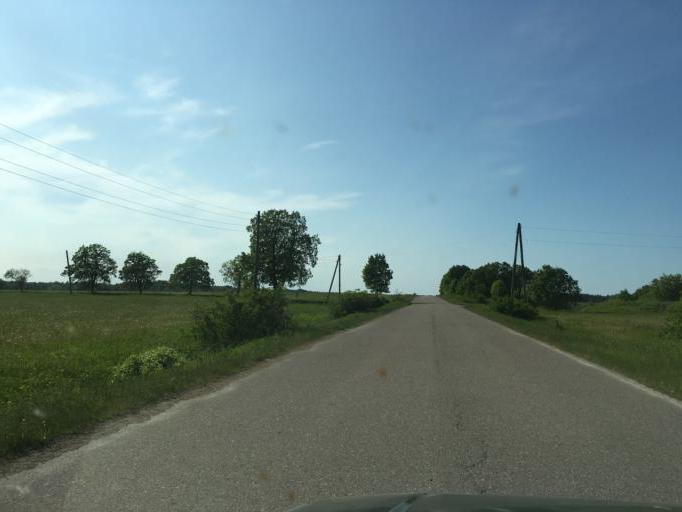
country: LV
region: Dundaga
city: Dundaga
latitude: 57.6094
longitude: 22.4434
